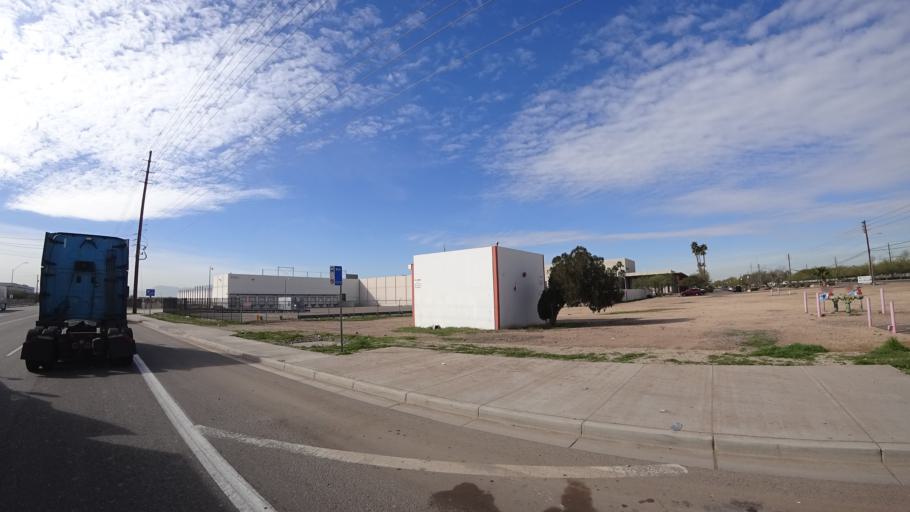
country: US
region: Arizona
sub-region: Maricopa County
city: Laveen
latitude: 33.4365
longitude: -112.1520
